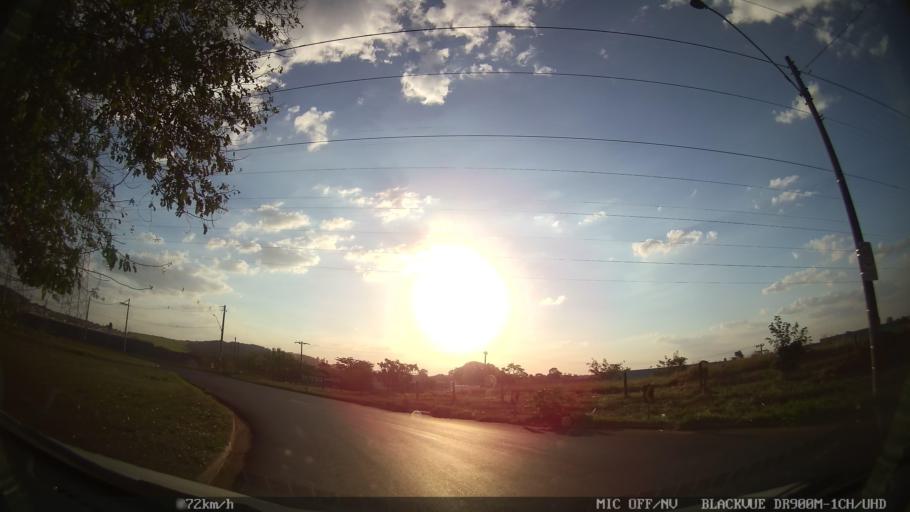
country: BR
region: Sao Paulo
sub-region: Ribeirao Preto
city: Ribeirao Preto
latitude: -21.1679
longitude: -47.7533
